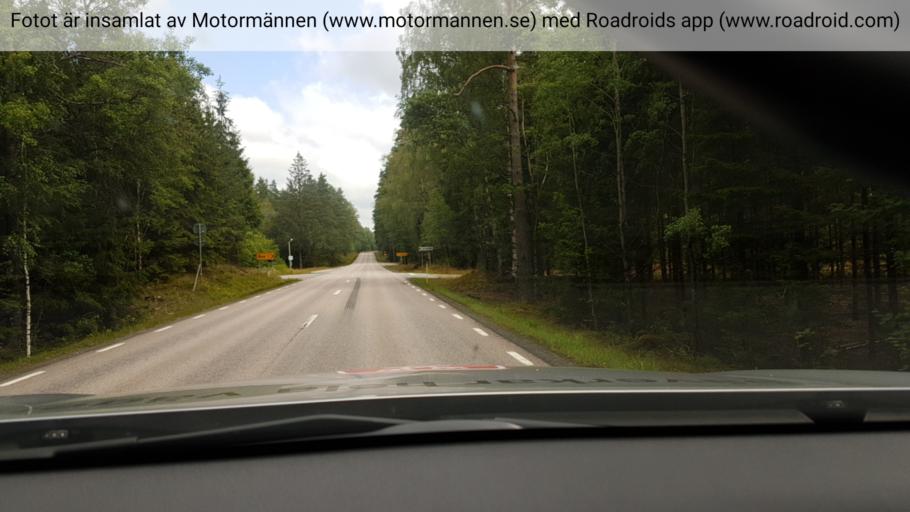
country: SE
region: Vaestra Goetaland
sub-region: Svenljunga Kommun
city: Svenljunga
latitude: 57.4879
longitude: 13.0608
